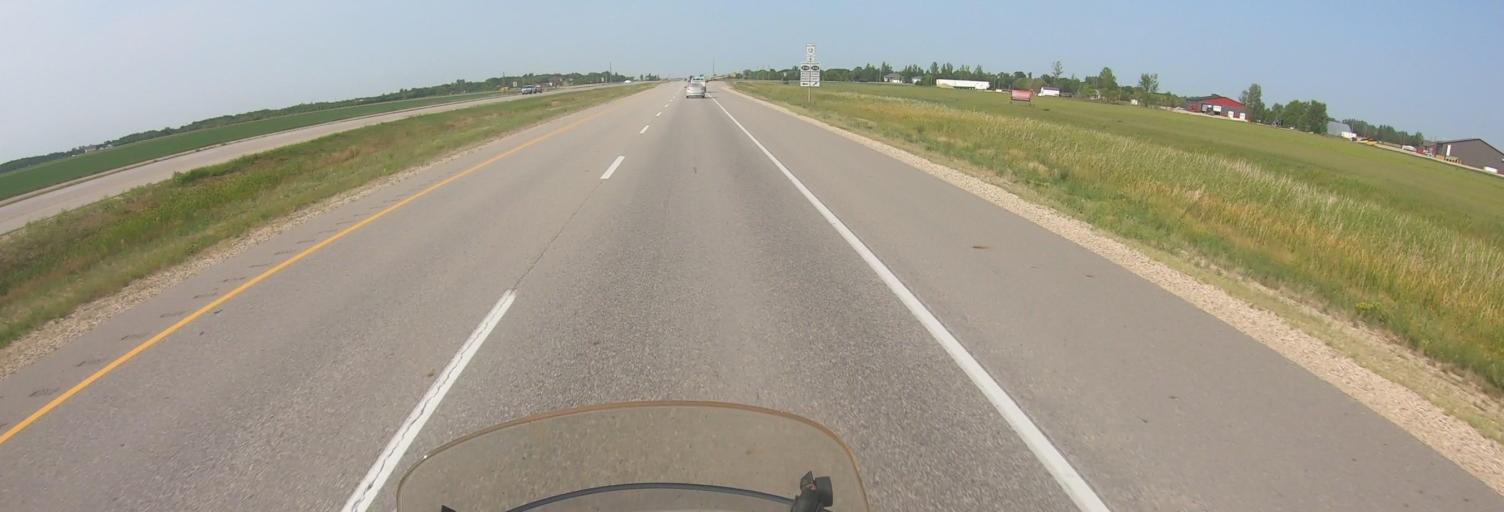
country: CA
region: Manitoba
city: Steinbach
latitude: 49.6613
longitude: -96.6685
